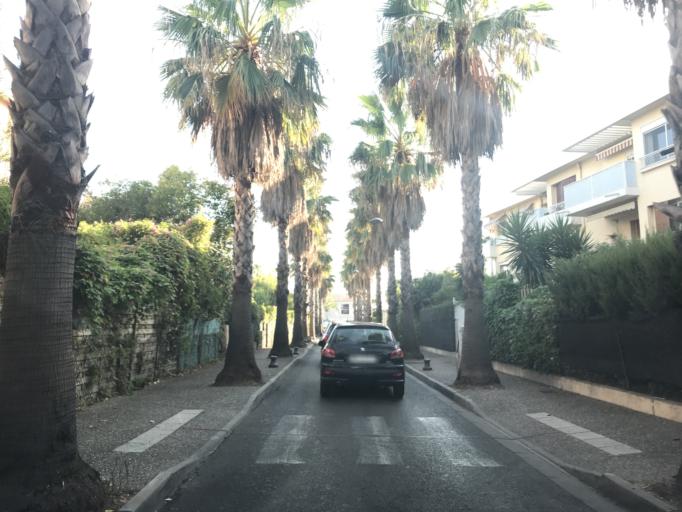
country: FR
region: Provence-Alpes-Cote d'Azur
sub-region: Departement du Var
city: Sanary-sur-Mer
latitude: 43.1164
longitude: 5.8090
